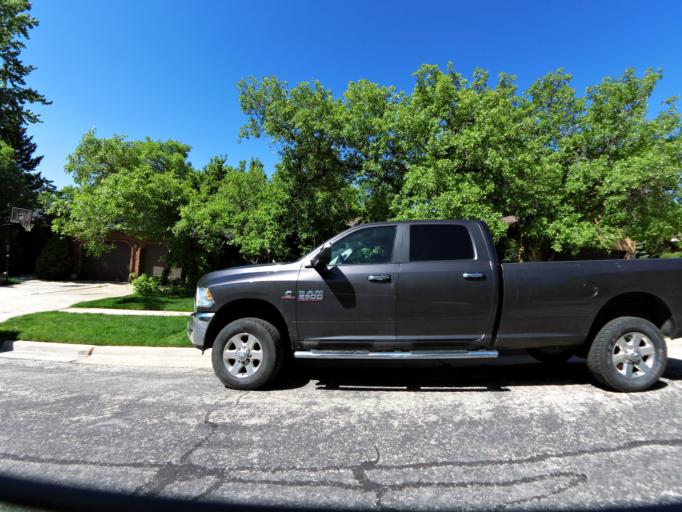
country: US
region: Utah
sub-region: Weber County
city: Uintah
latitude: 41.1715
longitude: -111.9316
